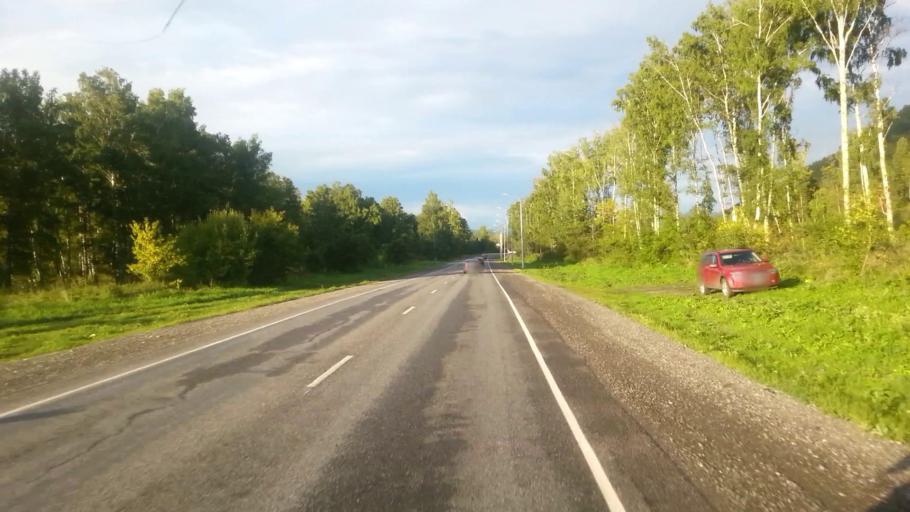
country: RU
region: Altay
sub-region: Mayminskiy Rayon
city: Manzherok
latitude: 51.8670
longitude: 85.7719
